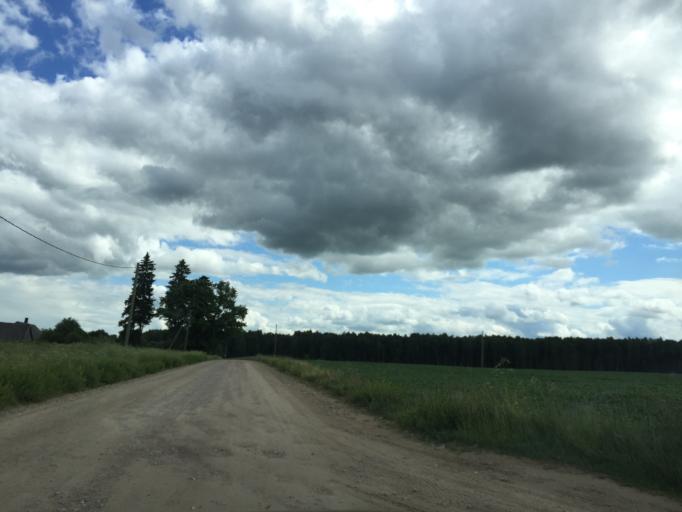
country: LV
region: Vecumnieki
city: Vecumnieki
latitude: 56.4696
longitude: 24.4232
